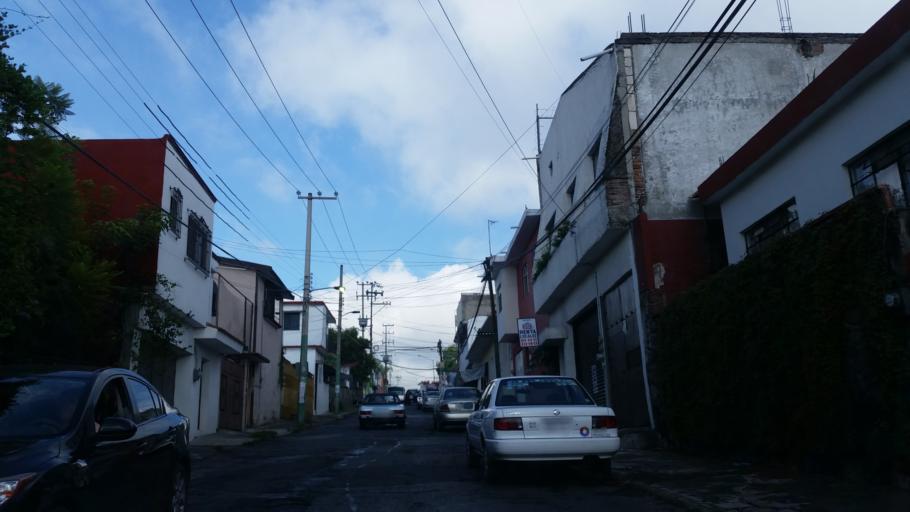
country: MX
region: Morelos
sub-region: Cuernavaca
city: Cuernavaca
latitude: 18.9203
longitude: -99.2109
